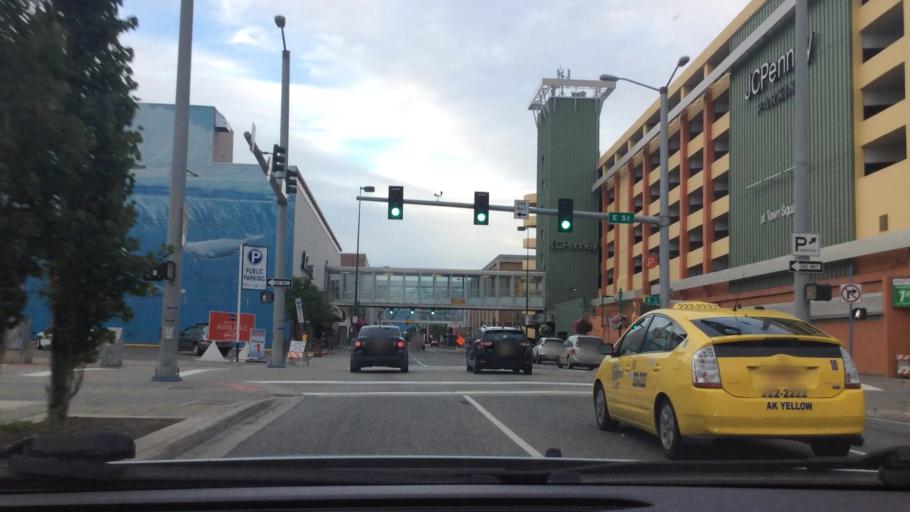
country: US
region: Alaska
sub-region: Anchorage Municipality
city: Anchorage
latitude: 61.2166
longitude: -149.8919
